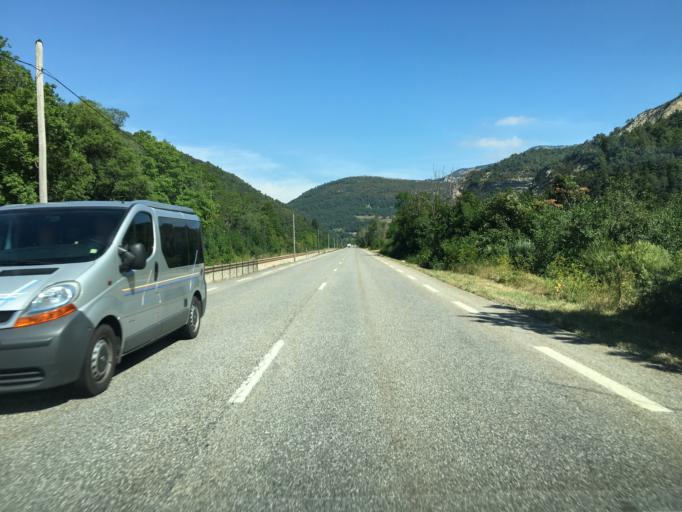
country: FR
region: Provence-Alpes-Cote d'Azur
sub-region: Departement des Hautes-Alpes
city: Veynes
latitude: 44.6027
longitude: 5.7087
